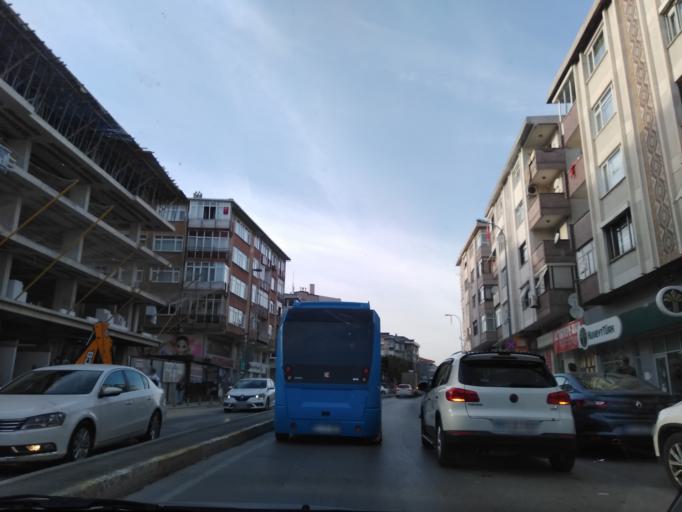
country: TR
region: Istanbul
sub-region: Atasehir
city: Atasehir
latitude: 40.9513
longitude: 29.1024
